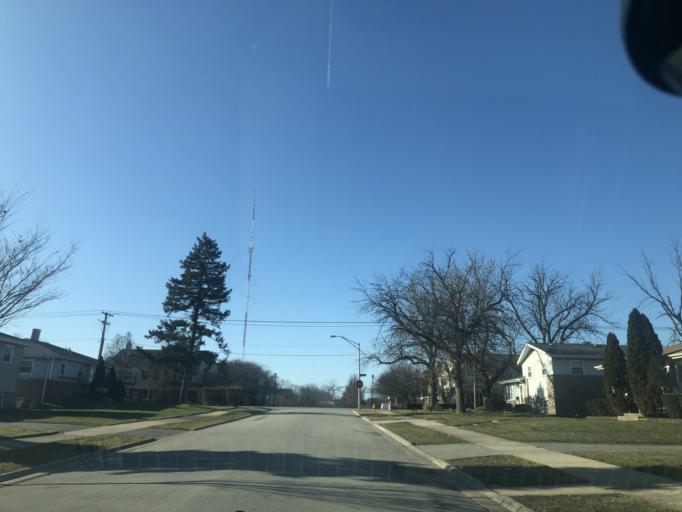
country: US
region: Illinois
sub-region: DuPage County
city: Addison
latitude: 41.9285
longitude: -88.0022
